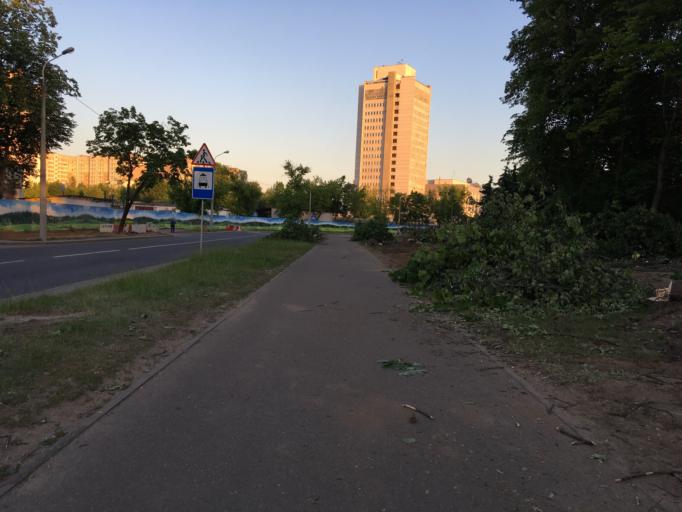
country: BY
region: Minsk
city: Minsk
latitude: 53.9259
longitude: 27.6276
